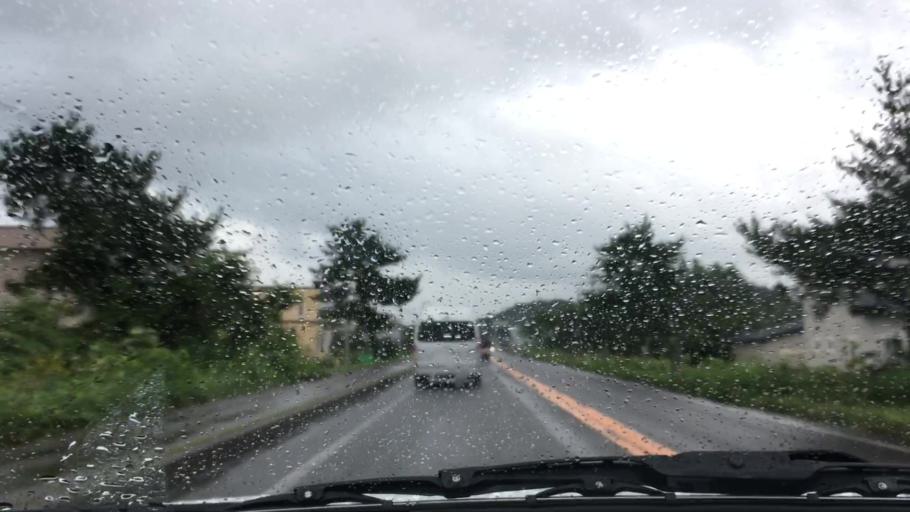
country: JP
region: Hokkaido
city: Nanae
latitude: 42.2332
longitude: 140.3233
